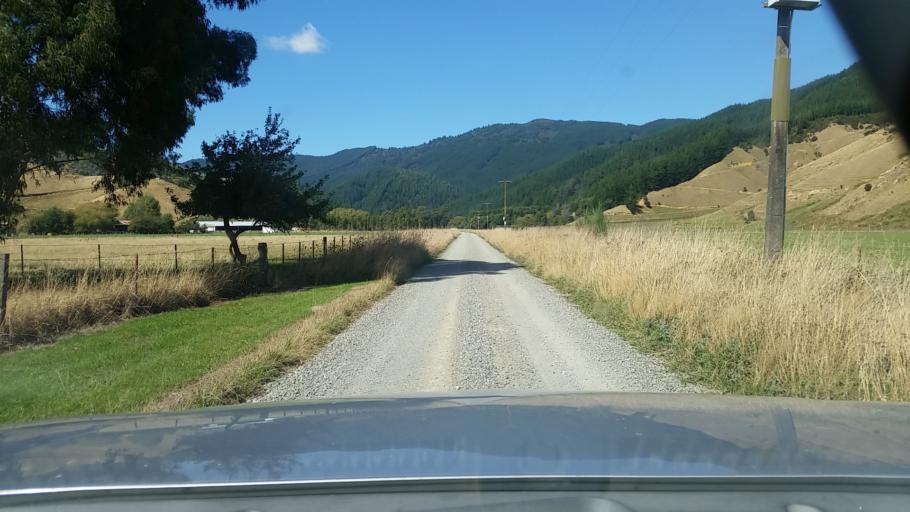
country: NZ
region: Marlborough
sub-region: Marlborough District
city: Blenheim
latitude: -41.4057
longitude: 173.7806
